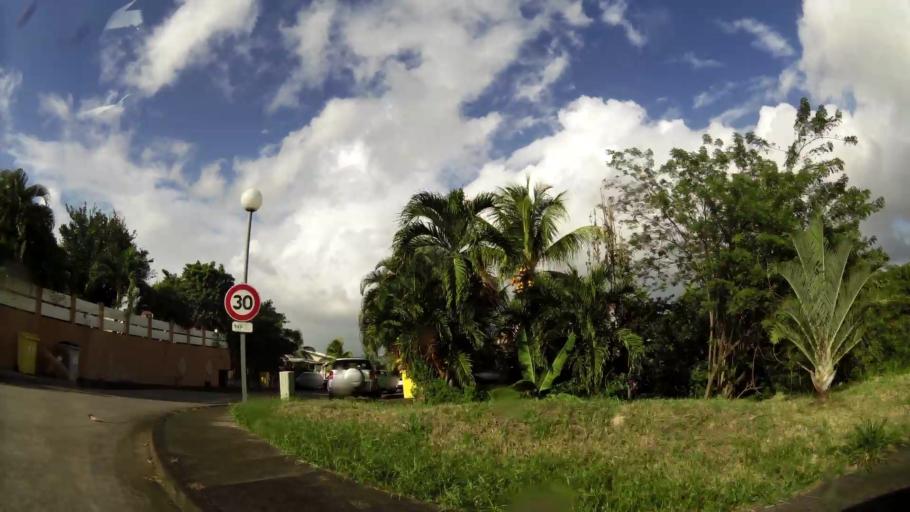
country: MQ
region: Martinique
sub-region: Martinique
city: Saint-Esprit
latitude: 14.5231
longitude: -60.9693
